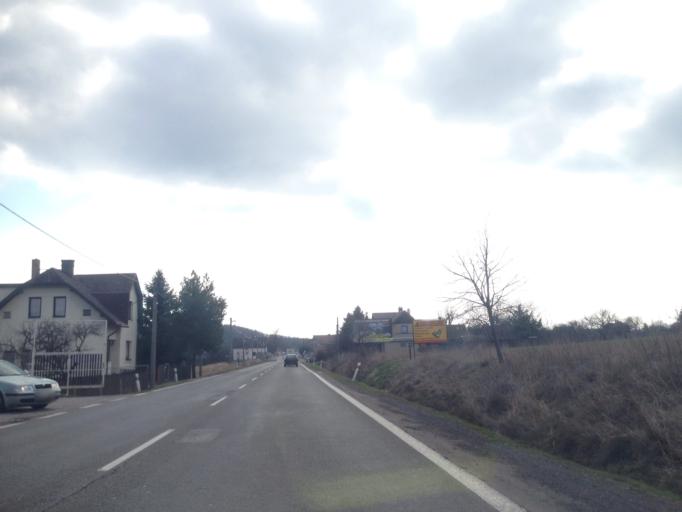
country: CZ
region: Kralovehradecky
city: Nova Paka
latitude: 50.4727
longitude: 15.5003
